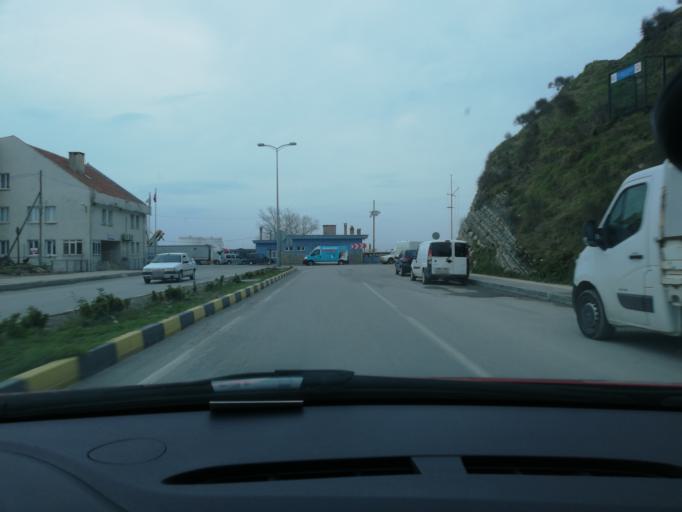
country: TR
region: Kastamonu
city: Inebolu
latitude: 41.9799
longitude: 33.7635
